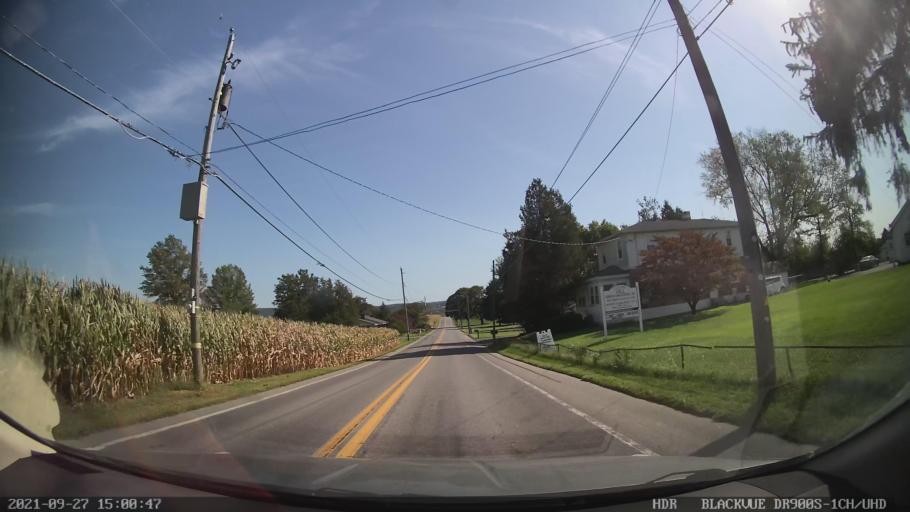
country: US
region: Pennsylvania
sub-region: Berks County
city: Kutztown
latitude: 40.5020
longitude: -75.7673
